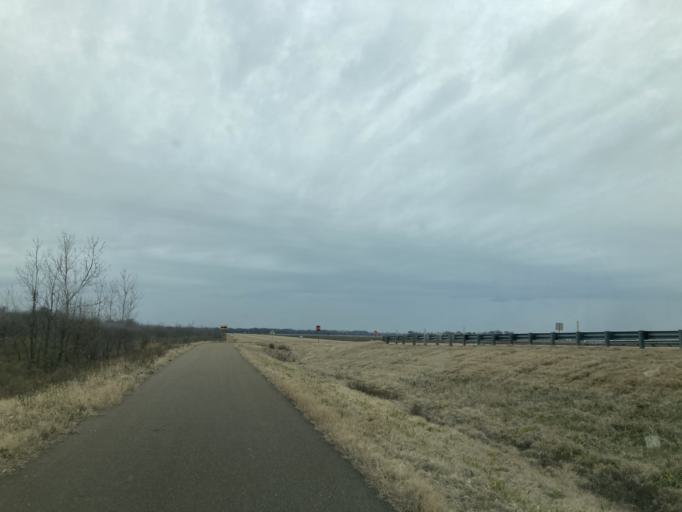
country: US
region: Mississippi
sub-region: Humphreys County
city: Belzoni
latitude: 33.0556
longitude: -90.4697
